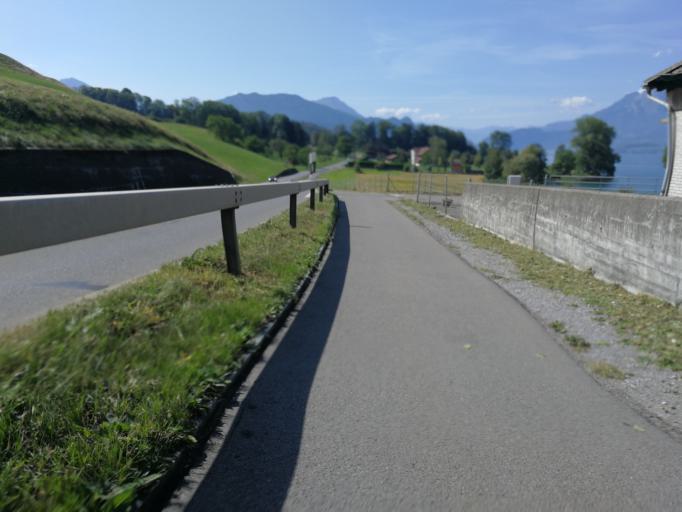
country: CH
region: Schwyz
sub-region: Bezirk Kuessnacht
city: Kussnacht
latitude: 47.0636
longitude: 8.4323
